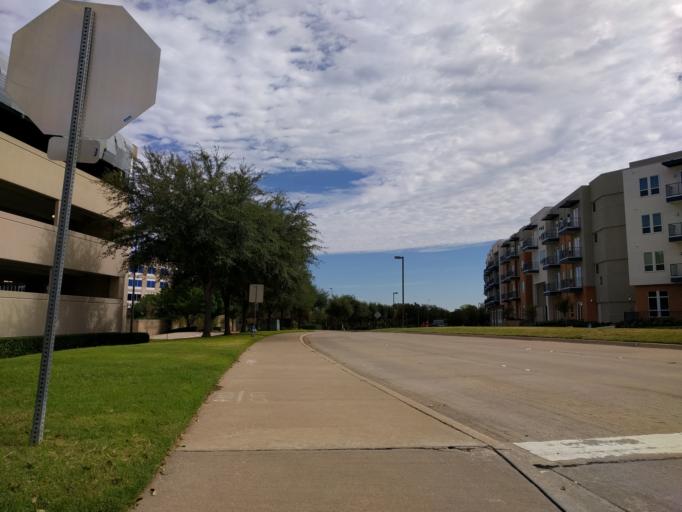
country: US
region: Texas
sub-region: Collin County
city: Plano
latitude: 32.9833
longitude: -96.7082
